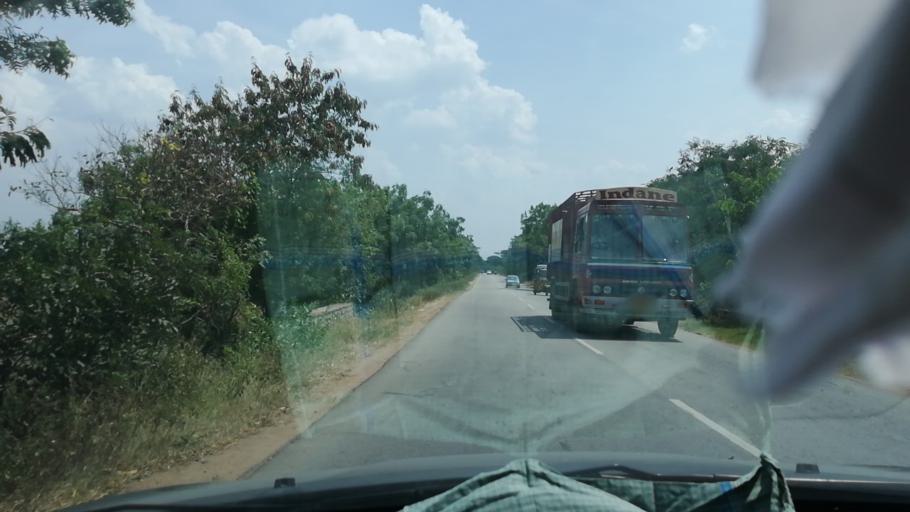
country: IN
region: Telangana
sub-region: Rangareddi
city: Secunderabad
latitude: 17.6362
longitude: 78.5583
